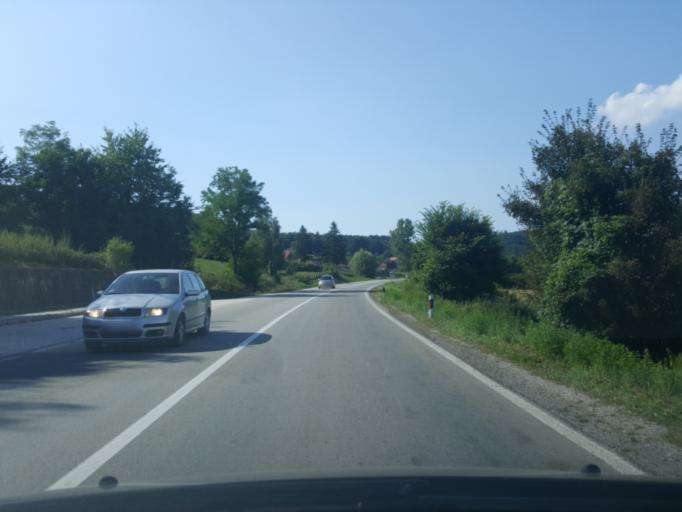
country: RS
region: Central Serbia
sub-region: Moravicki Okrug
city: Gornji Milanovac
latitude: 44.0839
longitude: 20.4807
